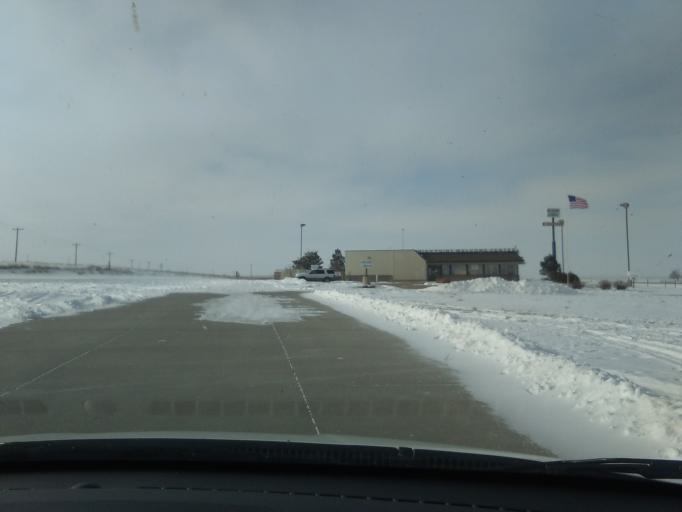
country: US
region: Nebraska
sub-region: Kimball County
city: Kimball
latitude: 41.2141
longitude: -103.6643
